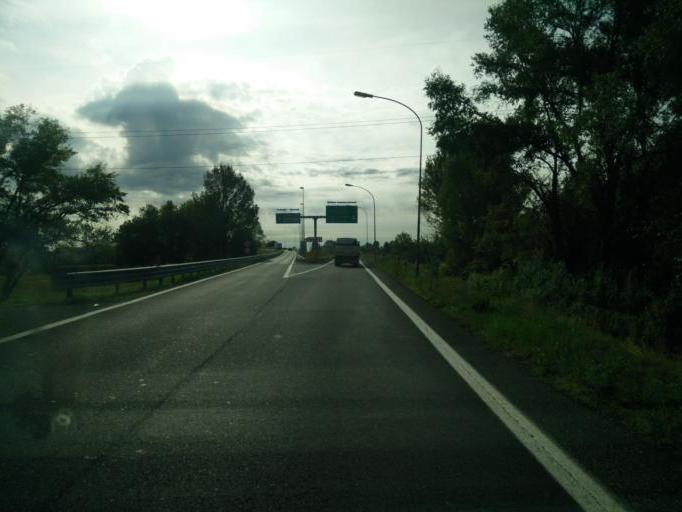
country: IT
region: Lombardy
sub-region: Provincia di Brescia
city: San Zeno Naviglio
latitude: 45.5052
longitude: 10.2340
